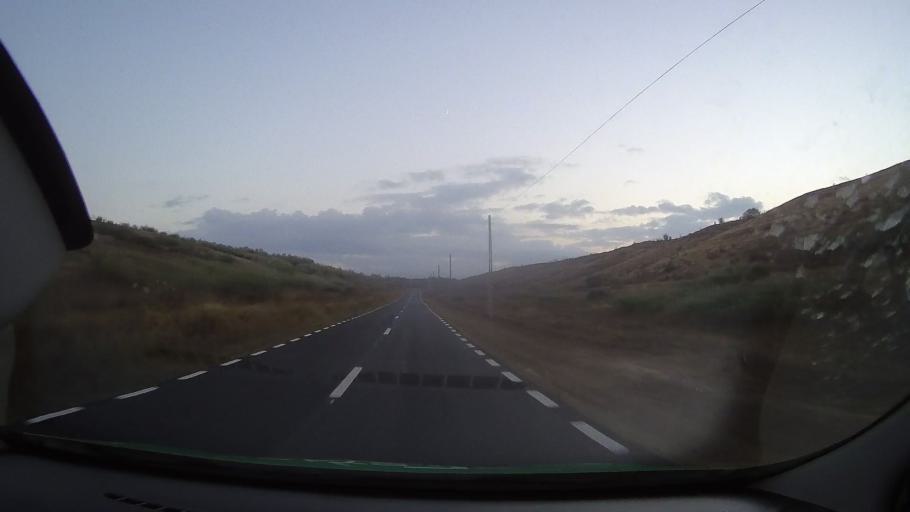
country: RO
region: Constanta
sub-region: Comuna Oltina
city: Oltina
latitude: 44.1428
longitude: 27.6659
